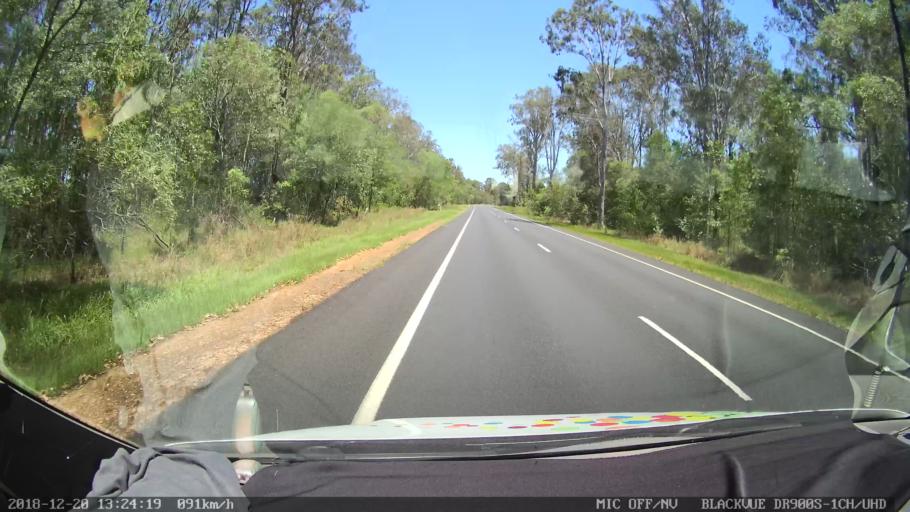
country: AU
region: New South Wales
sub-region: Richmond Valley
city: Casino
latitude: -29.1159
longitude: 153.0001
